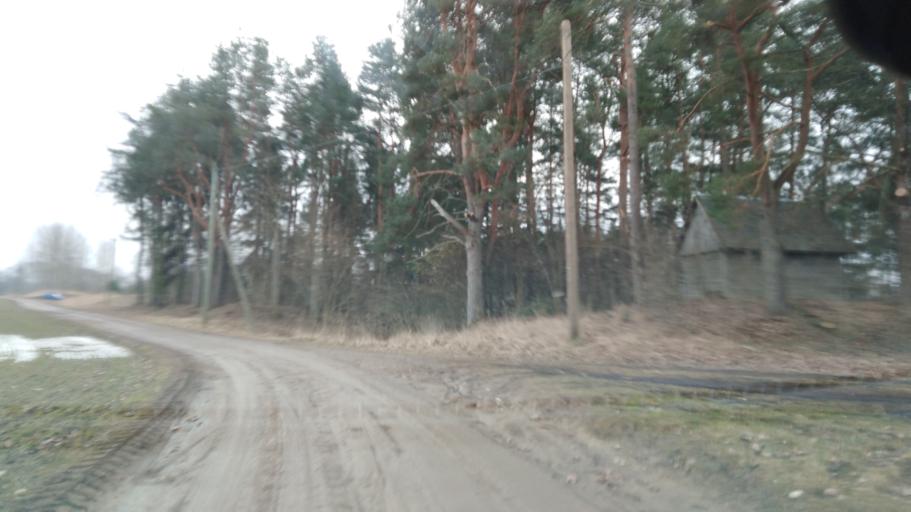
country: LV
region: Kuldigas Rajons
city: Kuldiga
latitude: 56.9851
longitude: 21.9616
